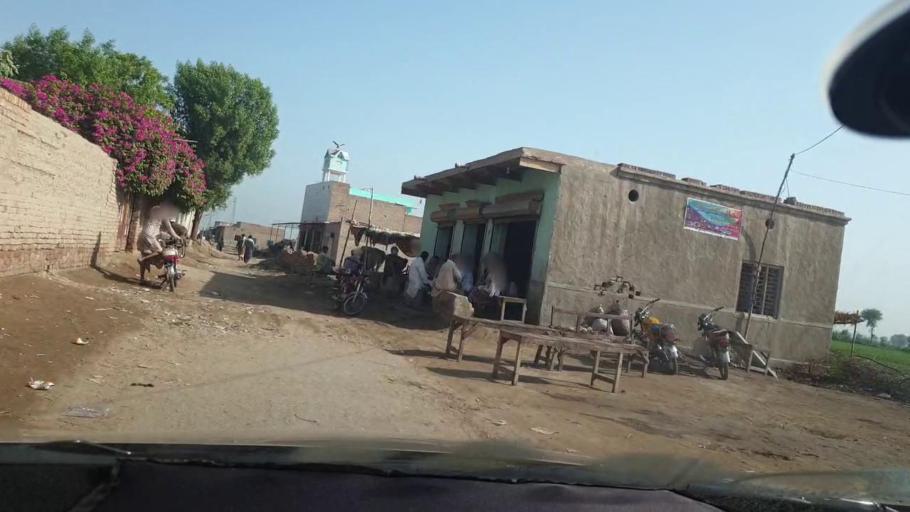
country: PK
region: Sindh
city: Kambar
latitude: 27.6614
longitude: 68.0140
